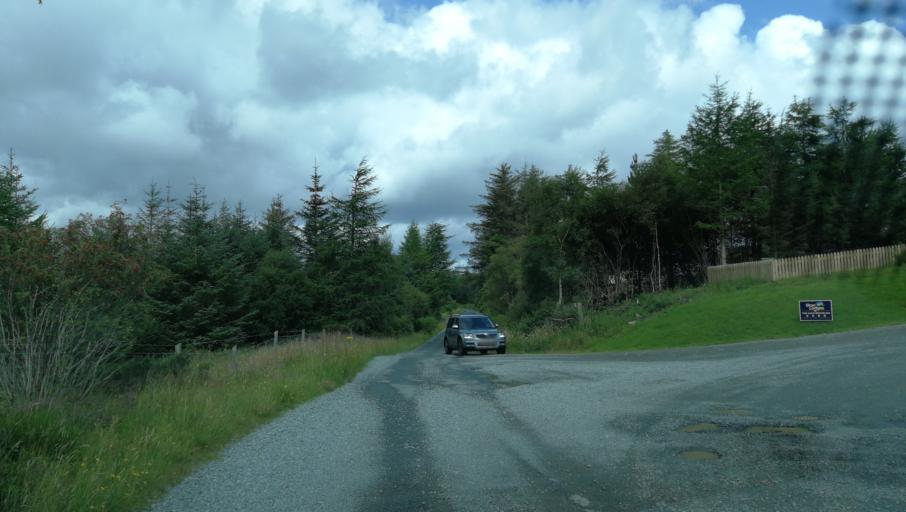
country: GB
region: Scotland
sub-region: Highland
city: Portree
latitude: 57.3796
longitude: -6.1951
